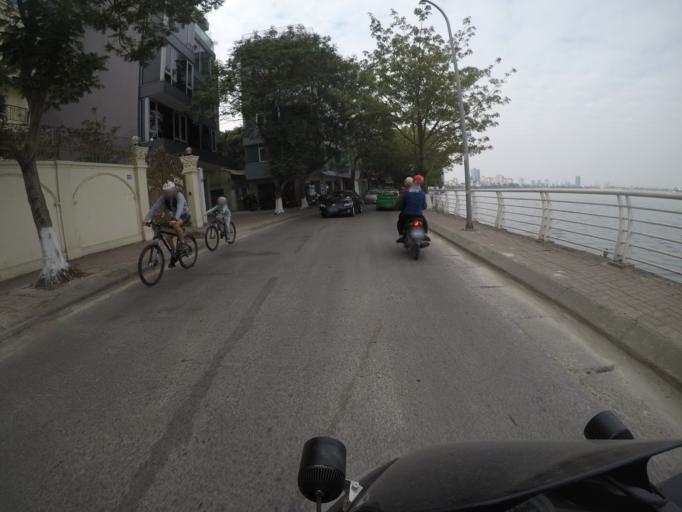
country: VN
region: Ha Noi
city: Tay Ho
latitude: 21.0537
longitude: 105.8122
